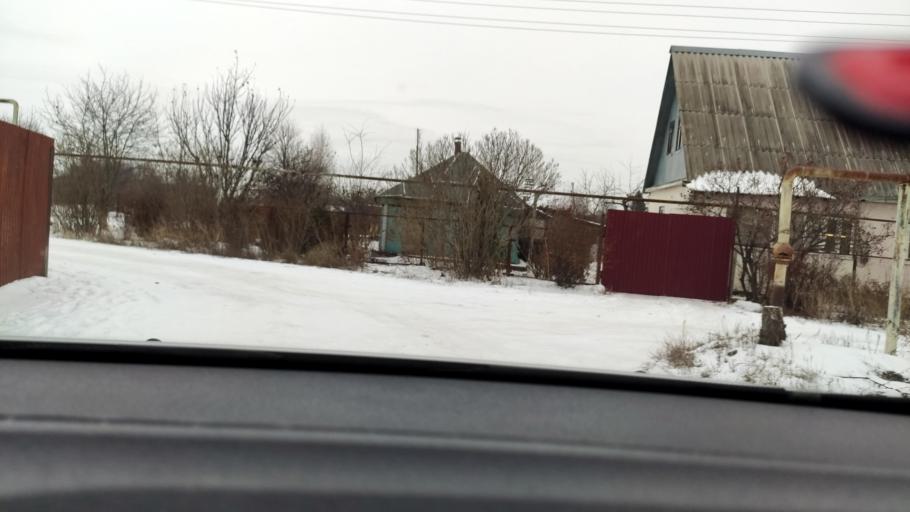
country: RU
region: Voronezj
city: Semiluki
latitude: 51.7016
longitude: 38.9977
